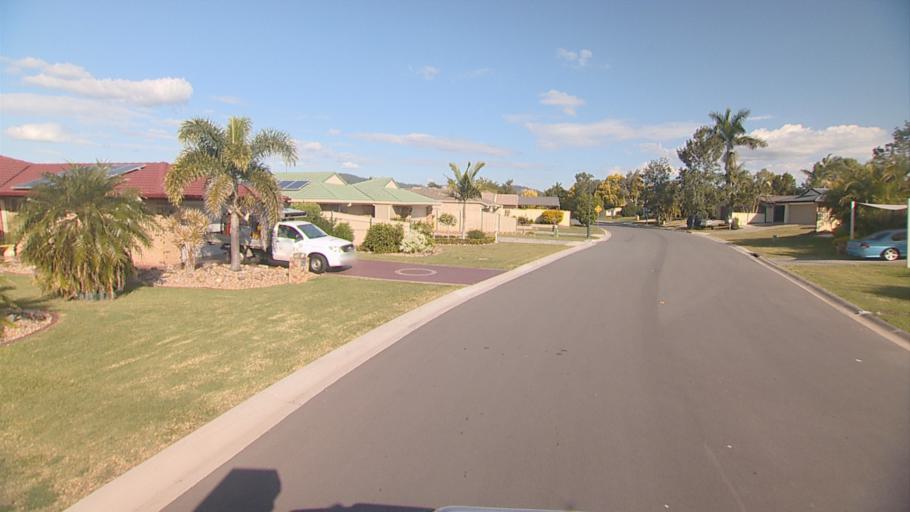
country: AU
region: Queensland
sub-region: Logan
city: Windaroo
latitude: -27.7493
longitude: 153.1945
